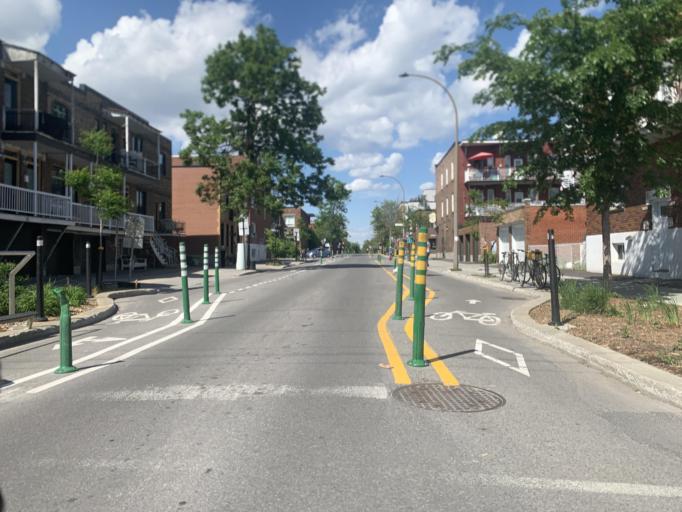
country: CA
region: Quebec
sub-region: Montreal
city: Montreal
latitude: 45.5427
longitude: -73.5922
